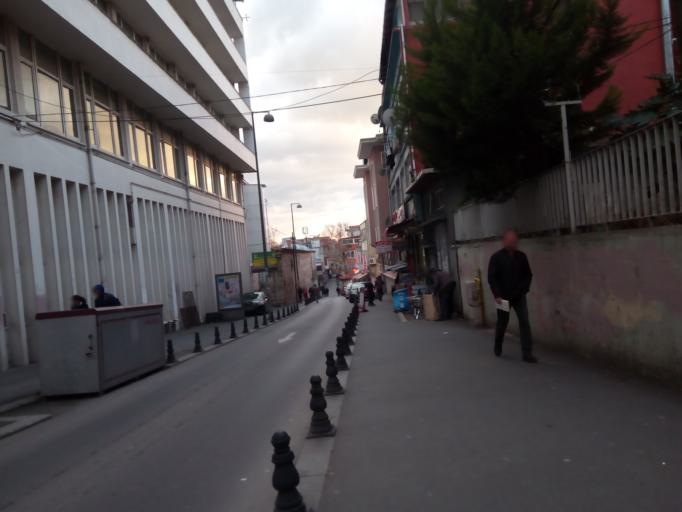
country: TR
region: Istanbul
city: Istanbul
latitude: 41.0142
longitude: 28.9622
